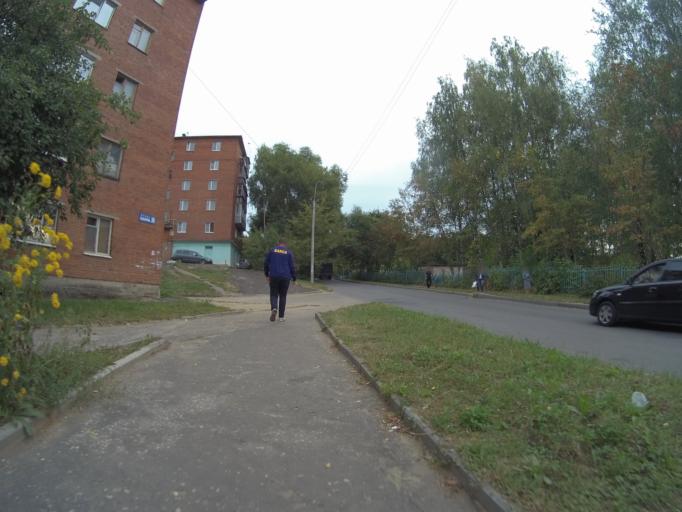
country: RU
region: Vladimir
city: Vladimir
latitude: 56.1251
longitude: 40.3538
